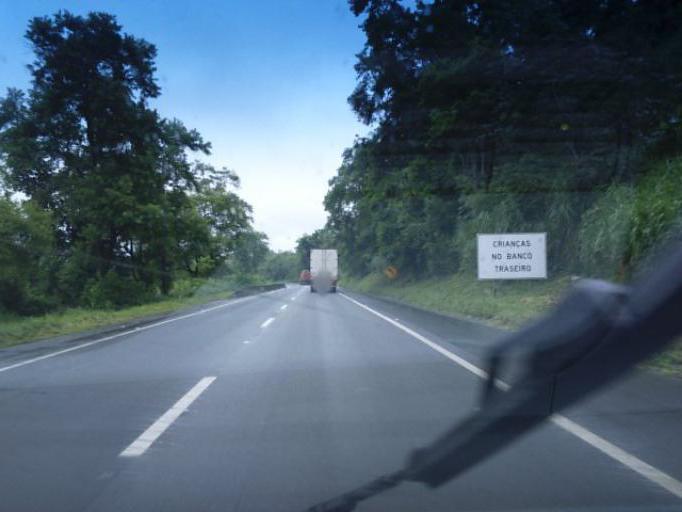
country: BR
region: Sao Paulo
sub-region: Cajati
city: Cajati
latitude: -24.7815
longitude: -48.1718
